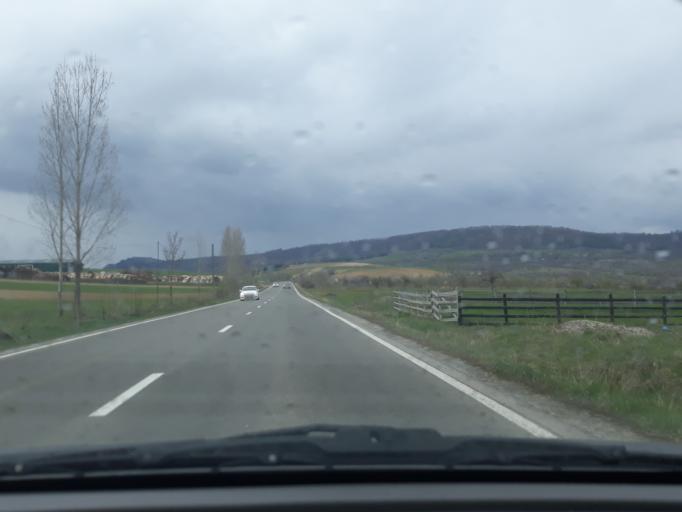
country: RO
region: Harghita
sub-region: Comuna Lupeni
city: Lupeni
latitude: 46.3879
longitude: 25.2166
